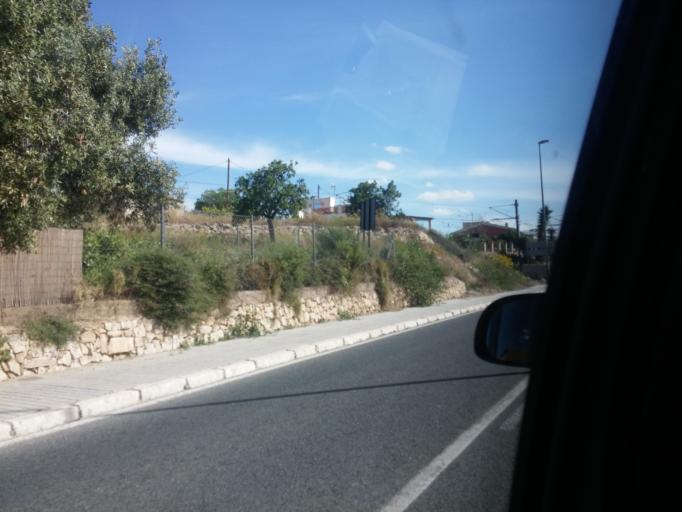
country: ES
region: Valencia
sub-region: Provincia de Alicante
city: Villajoyosa
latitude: 38.5137
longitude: -0.2171
